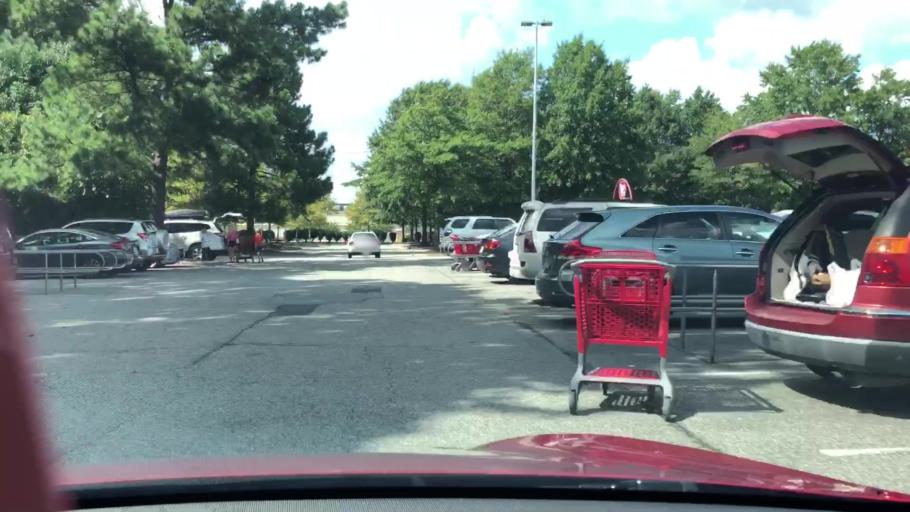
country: US
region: Virginia
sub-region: City of Virginia Beach
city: Virginia Beach
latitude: 36.8468
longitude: -76.0235
